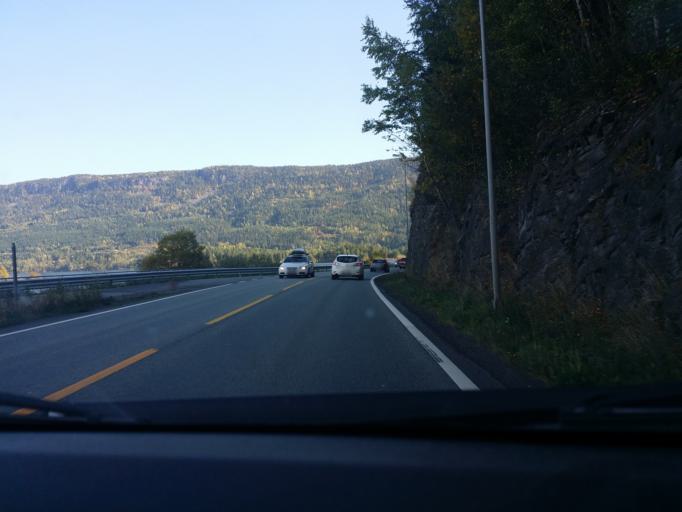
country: NO
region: Buskerud
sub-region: Hole
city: Vik
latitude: 60.0759
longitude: 10.2959
